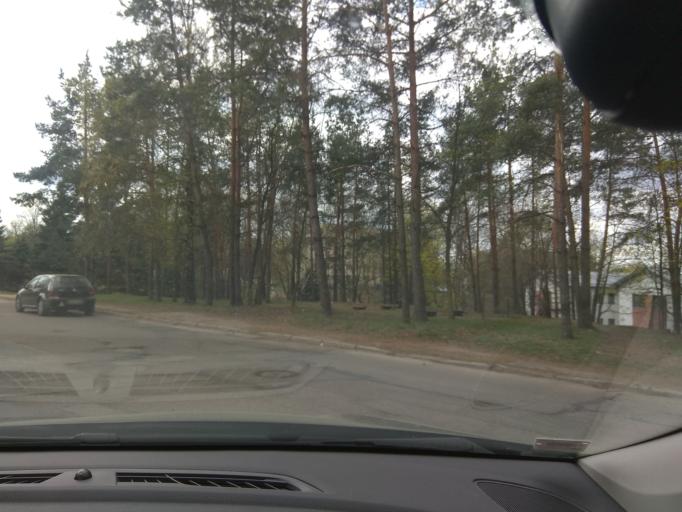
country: LT
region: Marijampoles apskritis
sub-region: Marijampole Municipality
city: Marijampole
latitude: 54.5714
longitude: 23.3610
